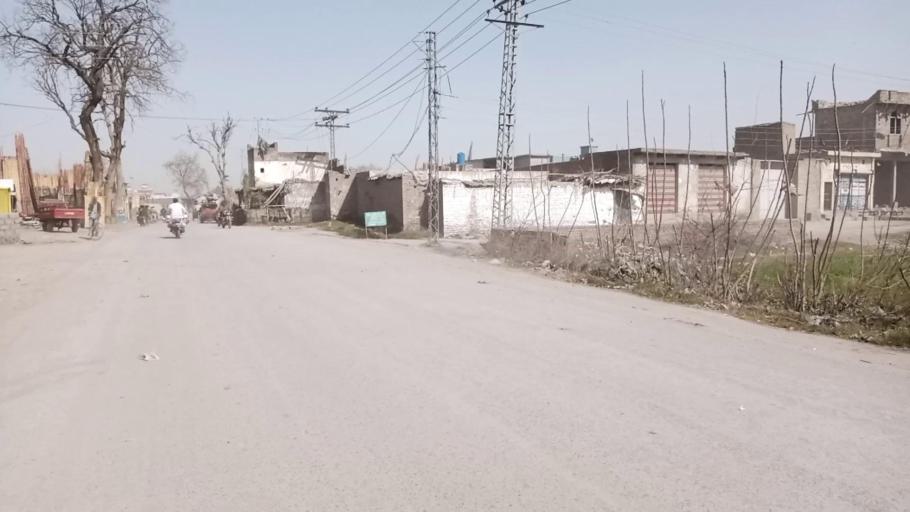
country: PK
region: Khyber Pakhtunkhwa
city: Peshawar
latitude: 33.9956
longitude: 71.6338
